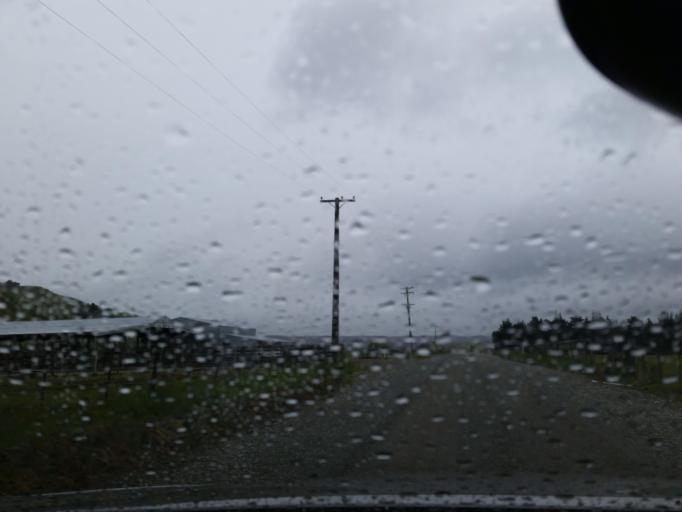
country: NZ
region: Southland
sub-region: Southland District
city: Riverton
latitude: -45.9850
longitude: 167.5810
